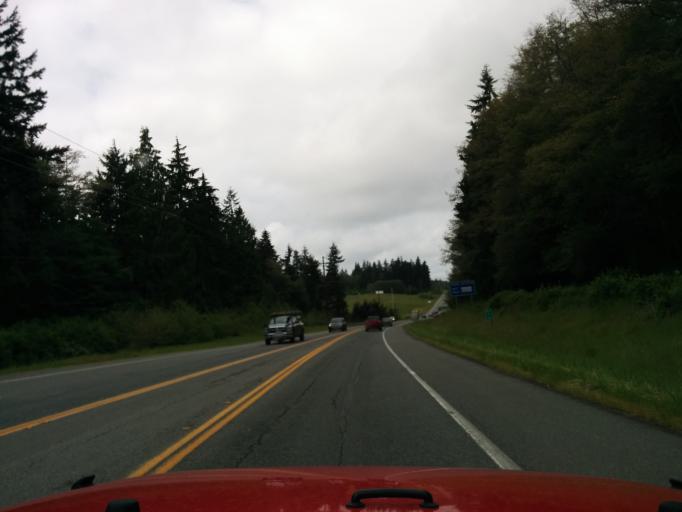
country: US
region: Washington
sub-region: Island County
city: Freeland
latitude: 48.0067
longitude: -122.4857
